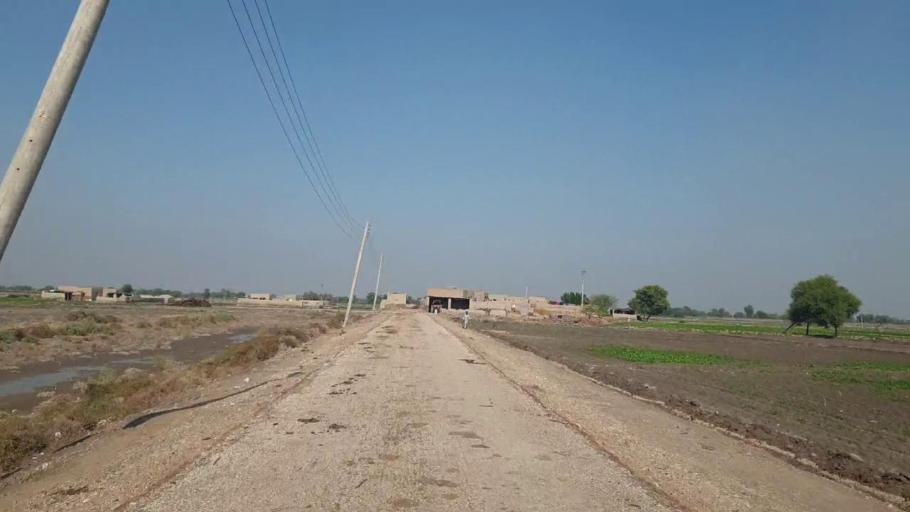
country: PK
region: Sindh
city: Sehwan
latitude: 26.4236
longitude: 67.8103
